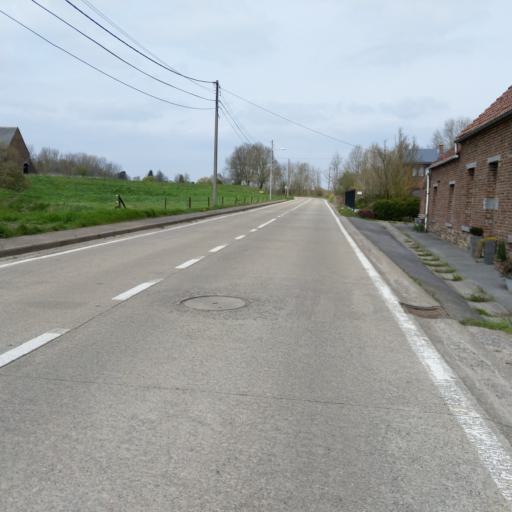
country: BE
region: Wallonia
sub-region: Province du Hainaut
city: Quevy-le-Petit
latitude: 50.3630
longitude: 3.9471
